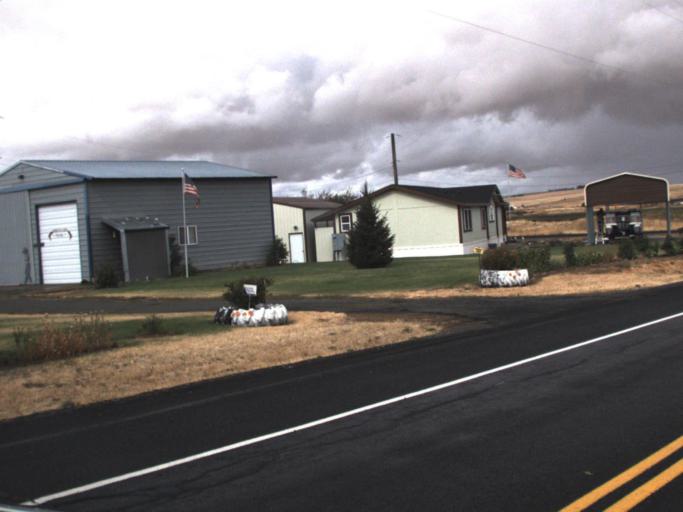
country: US
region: Washington
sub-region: Spokane County
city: Medical Lake
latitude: 47.6726
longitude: -117.8780
